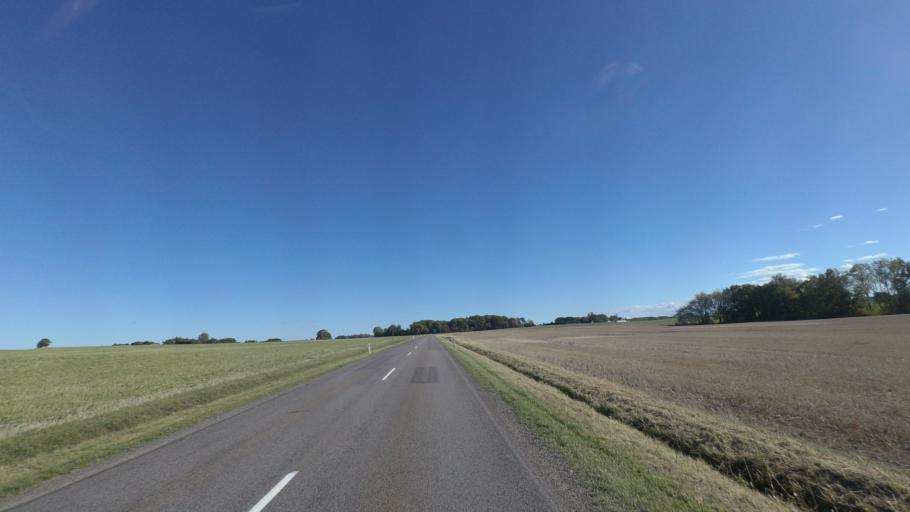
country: DK
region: Capital Region
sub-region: Bornholm Kommune
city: Nexo
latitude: 55.1224
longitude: 15.0961
